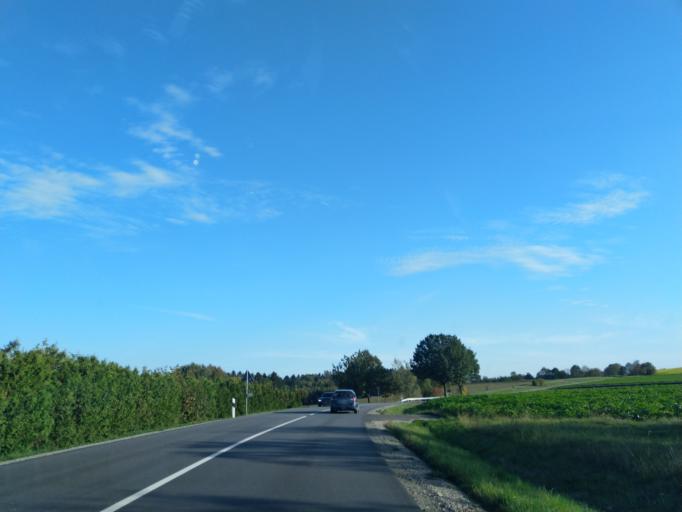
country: DE
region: Bavaria
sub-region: Lower Bavaria
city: Metten
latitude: 48.8665
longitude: 12.9354
